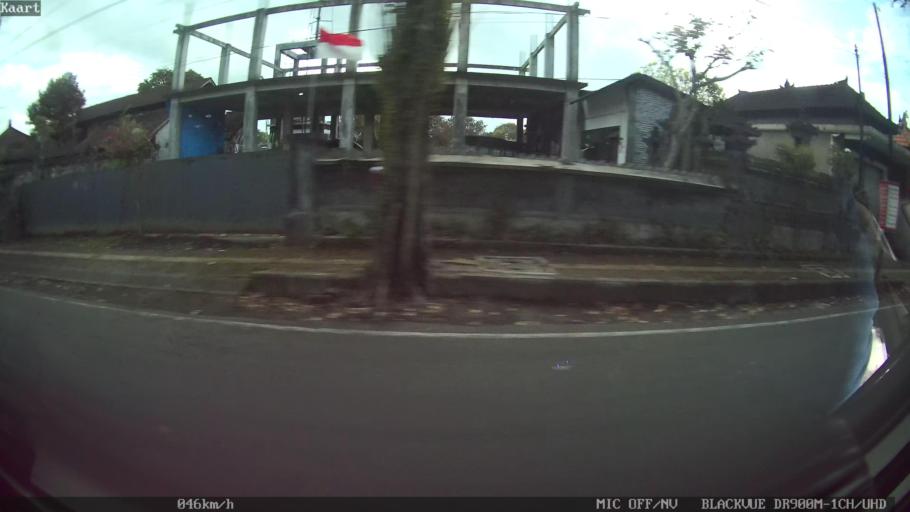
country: ID
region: Bali
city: Banjar Jambe Baleran
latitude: -8.5358
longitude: 115.1247
